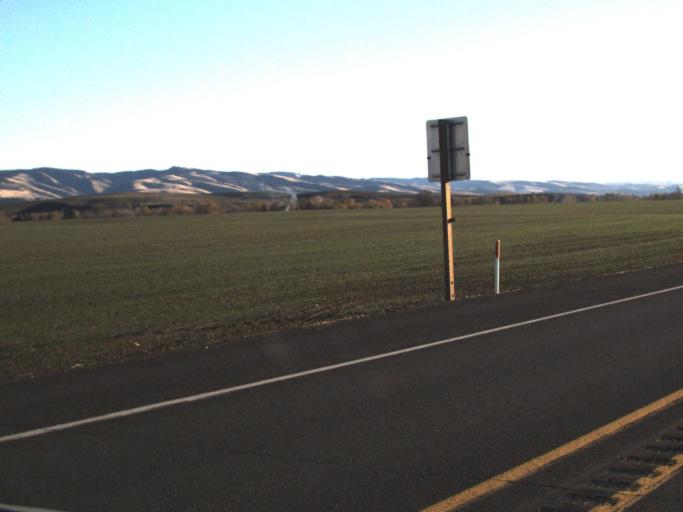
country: US
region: Washington
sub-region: Walla Walla County
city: Walla Walla East
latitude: 46.0972
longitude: -118.2546
